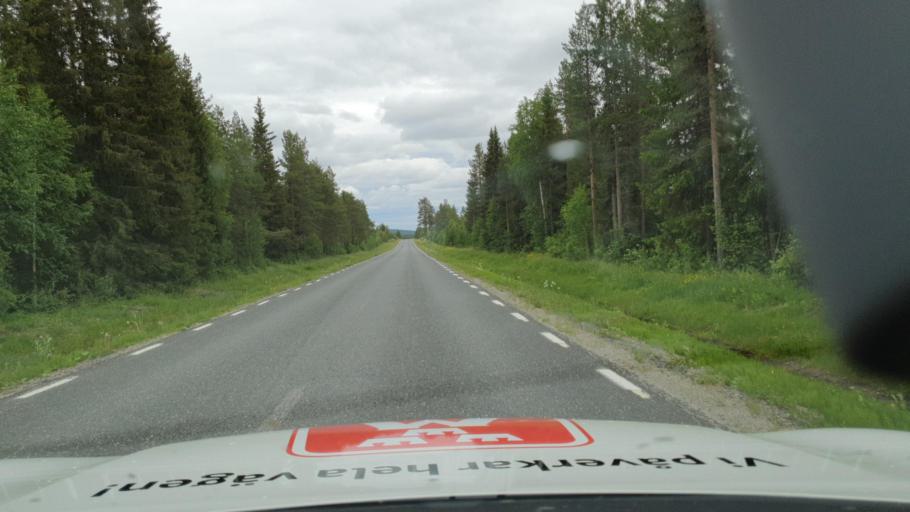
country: SE
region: Vaesterbotten
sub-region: Lycksele Kommun
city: Soderfors
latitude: 64.2867
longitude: 18.1853
